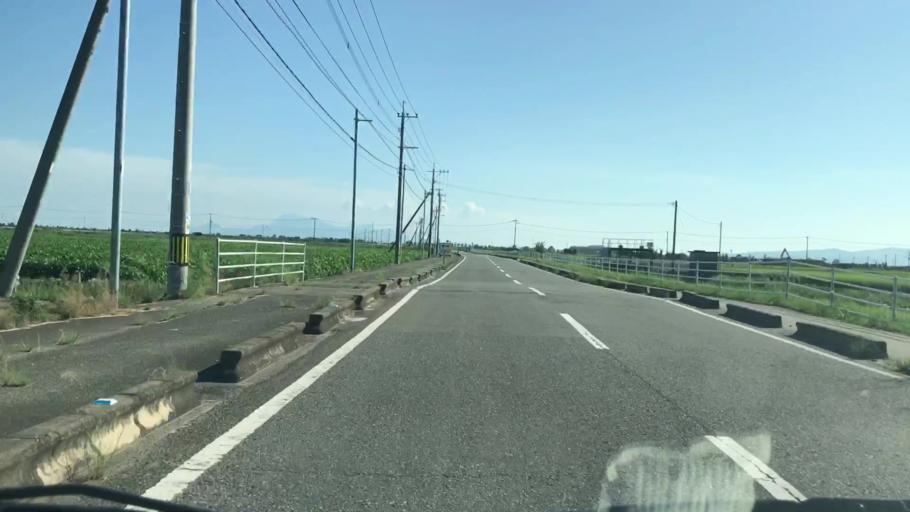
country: JP
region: Saga Prefecture
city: Okawa
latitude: 33.1675
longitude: 130.3095
